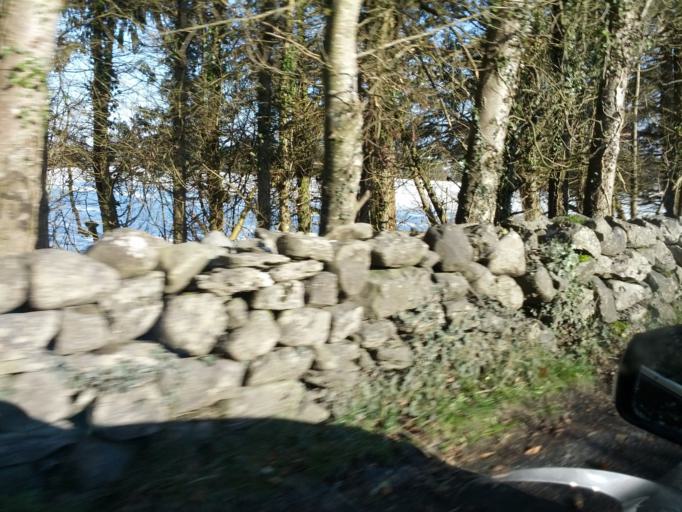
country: IE
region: Connaught
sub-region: County Galway
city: Athenry
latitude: 53.1953
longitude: -8.7961
